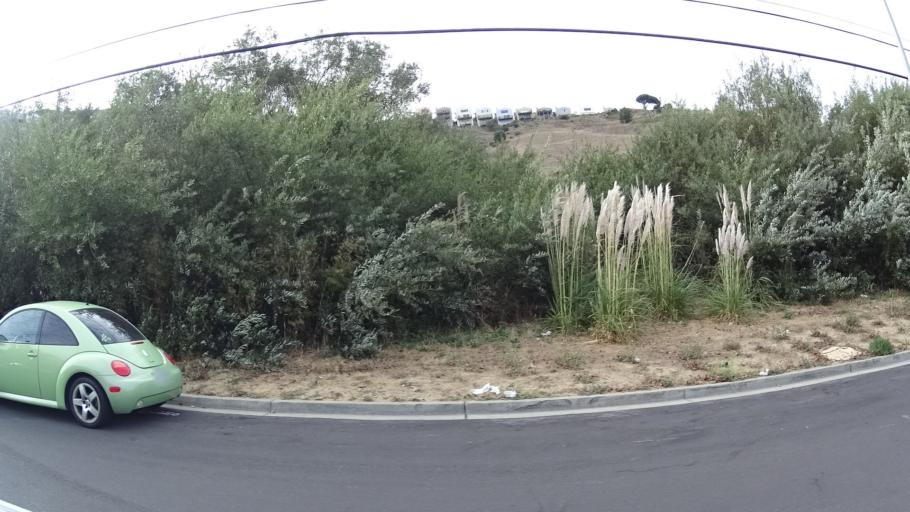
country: US
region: California
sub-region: San Mateo County
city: Brisbane
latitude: 37.7045
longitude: -122.4256
